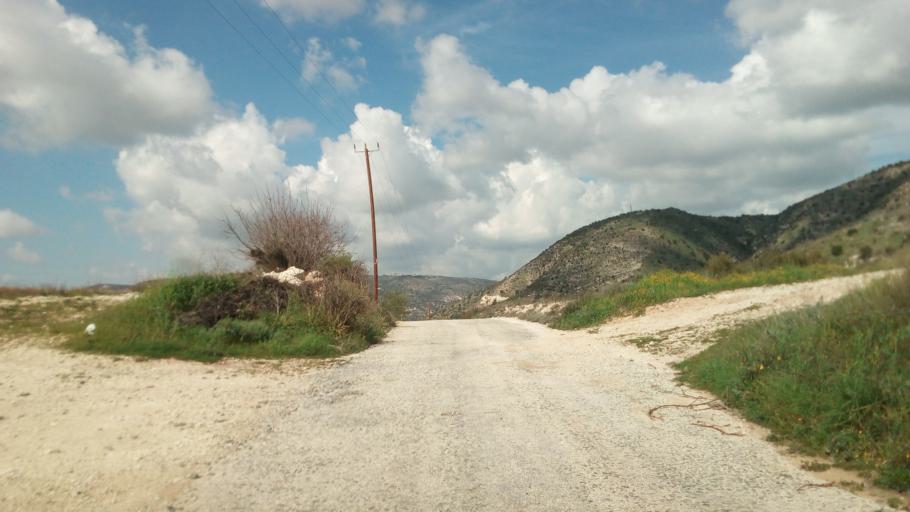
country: CY
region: Pafos
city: Mesogi
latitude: 34.7863
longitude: 32.5455
